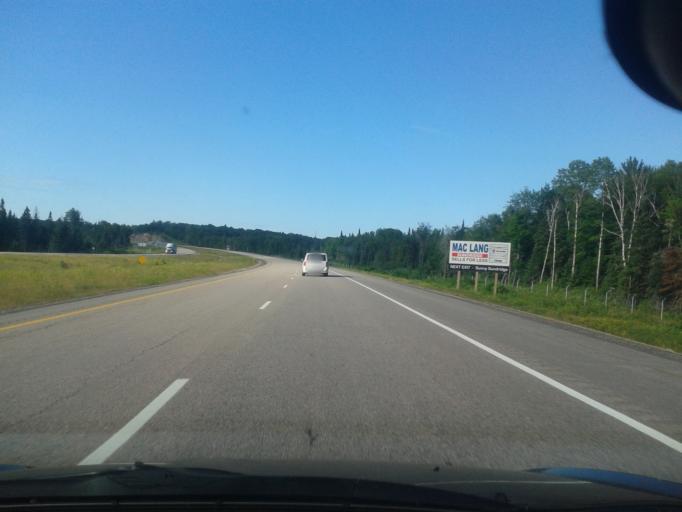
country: CA
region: Ontario
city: South River
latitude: 45.8086
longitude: -79.4106
